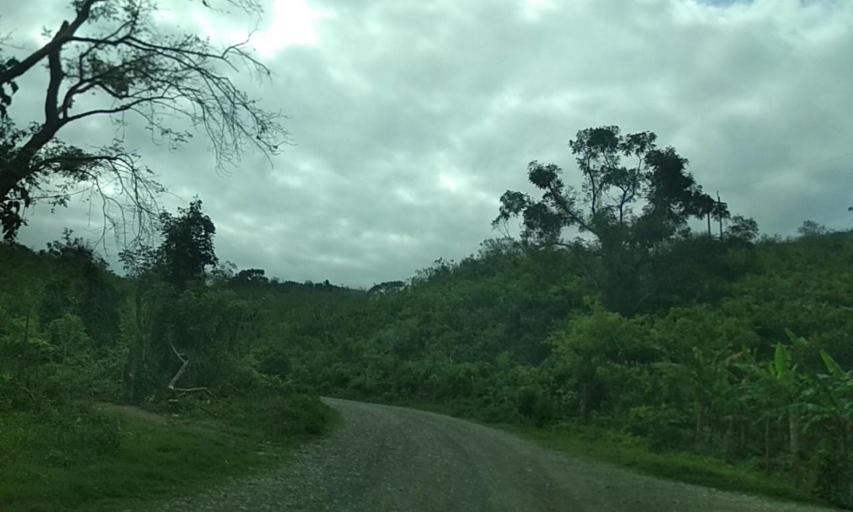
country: MX
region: Veracruz
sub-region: Papantla
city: Residencial Tajin
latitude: 20.6161
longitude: -97.3612
